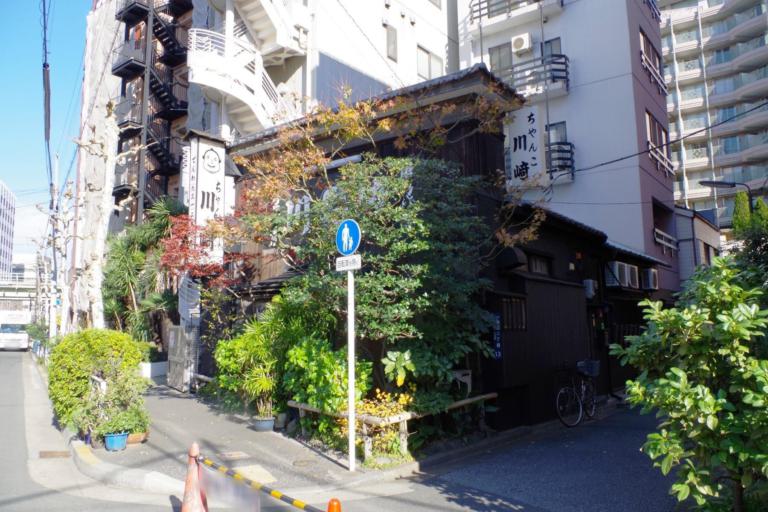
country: JP
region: Tokyo
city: Tokyo
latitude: 35.6953
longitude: 139.7913
